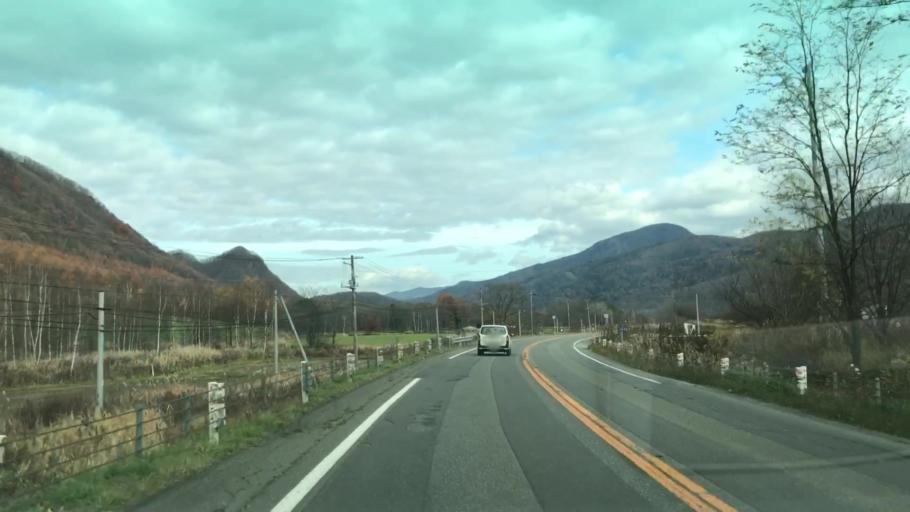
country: JP
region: Hokkaido
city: Shizunai-furukawacho
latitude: 42.7671
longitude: 142.3746
